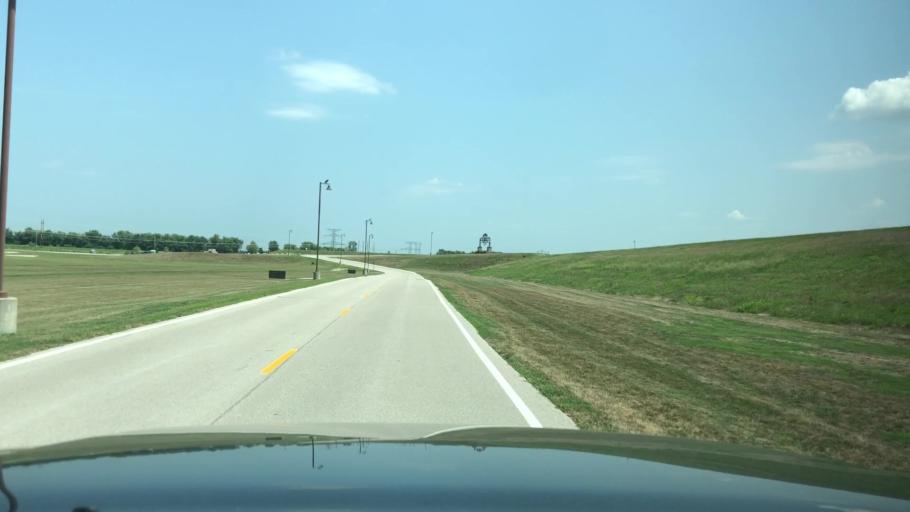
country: US
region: Missouri
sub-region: Saint Charles County
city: Saint Peters
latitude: 38.8212
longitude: -90.5672
